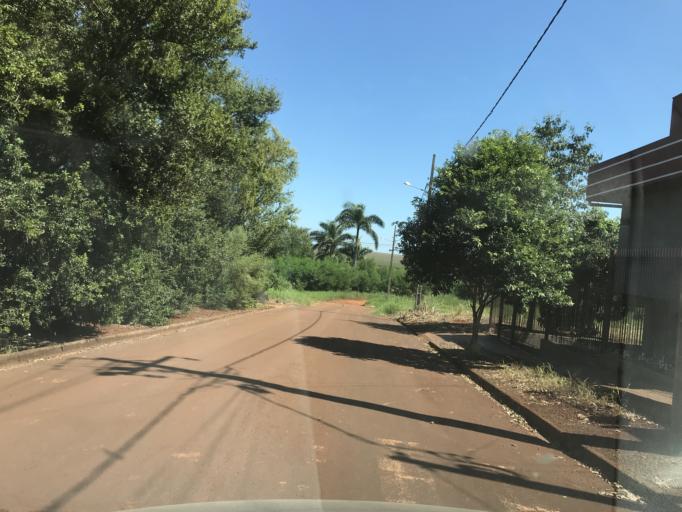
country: BR
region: Parana
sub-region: Palotina
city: Palotina
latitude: -24.2977
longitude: -53.8462
